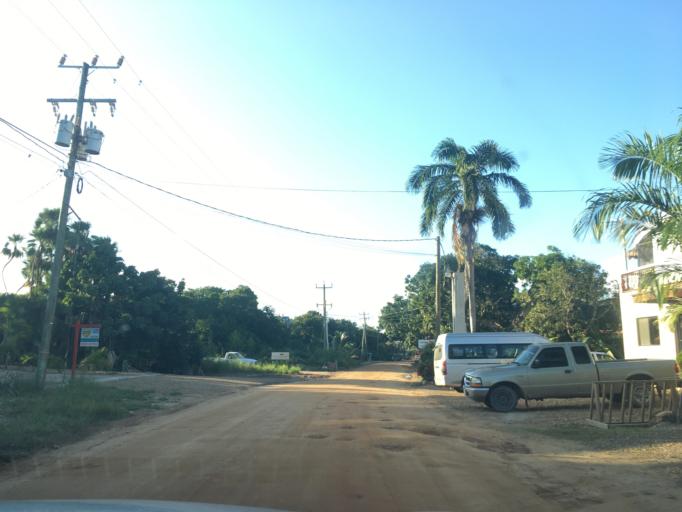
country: BZ
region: Stann Creek
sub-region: Dangriga
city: Dangriga
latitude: 16.8375
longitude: -88.2692
